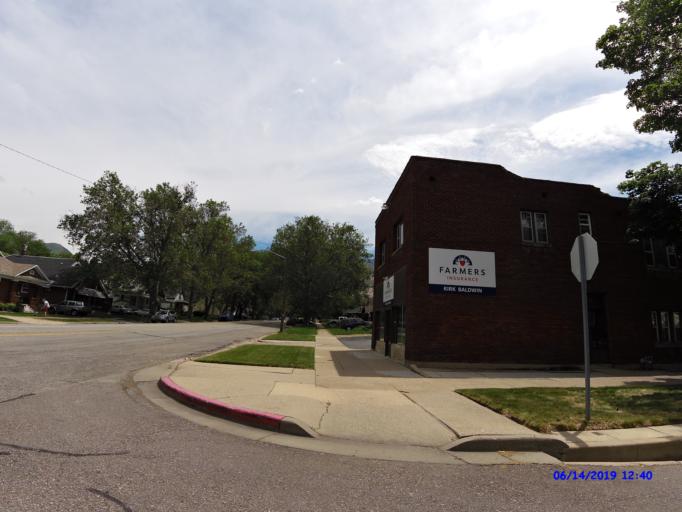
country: US
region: Utah
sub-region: Weber County
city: Ogden
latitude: 41.2224
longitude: -111.9537
